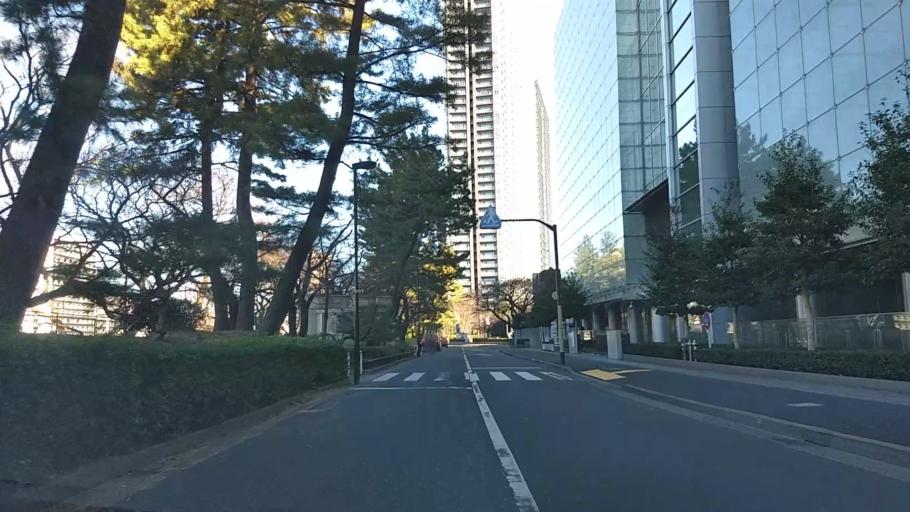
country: JP
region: Tokyo
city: Tokyo
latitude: 35.6961
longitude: 139.7408
